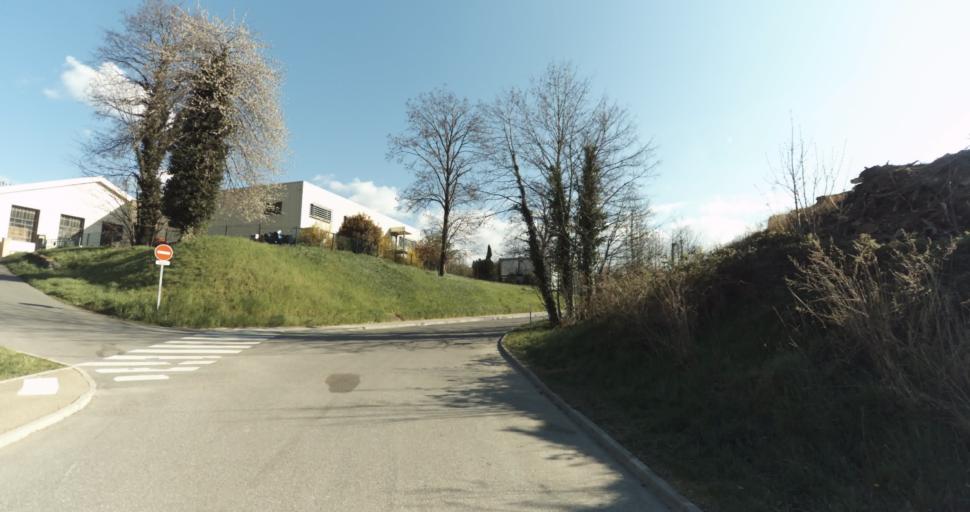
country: FR
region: Rhone-Alpes
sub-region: Departement de la Loire
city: Saint-Jean-Bonnefonds
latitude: 45.4680
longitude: 4.4430
